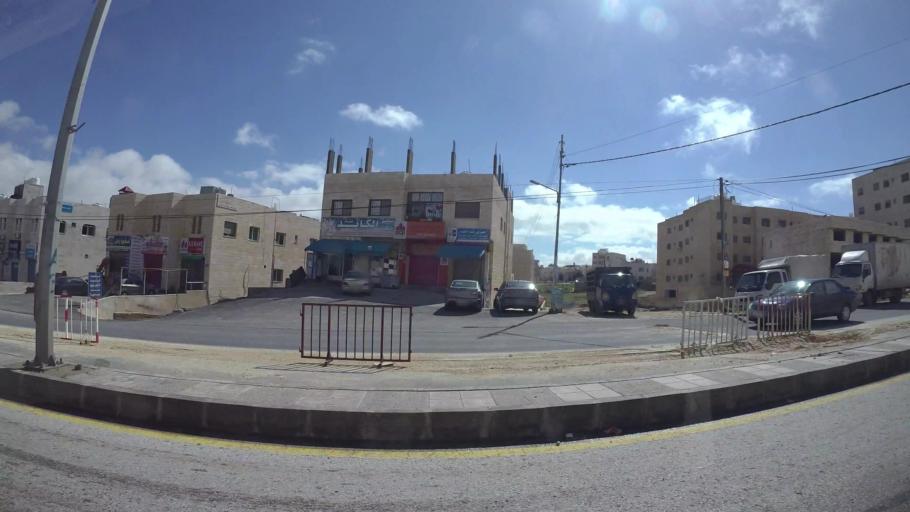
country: JO
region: Amman
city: Al Jubayhah
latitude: 32.0574
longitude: 35.8920
